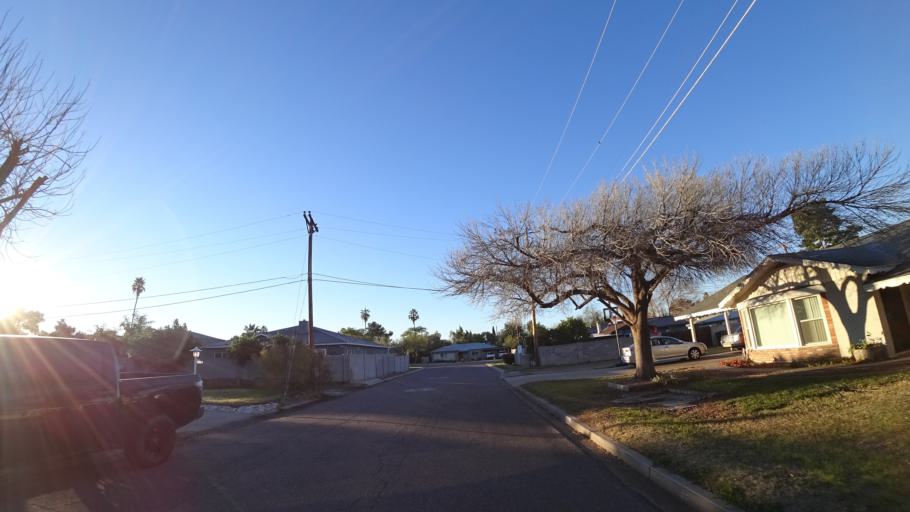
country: US
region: Arizona
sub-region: Maricopa County
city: Paradise Valley
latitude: 33.4847
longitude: -111.9934
